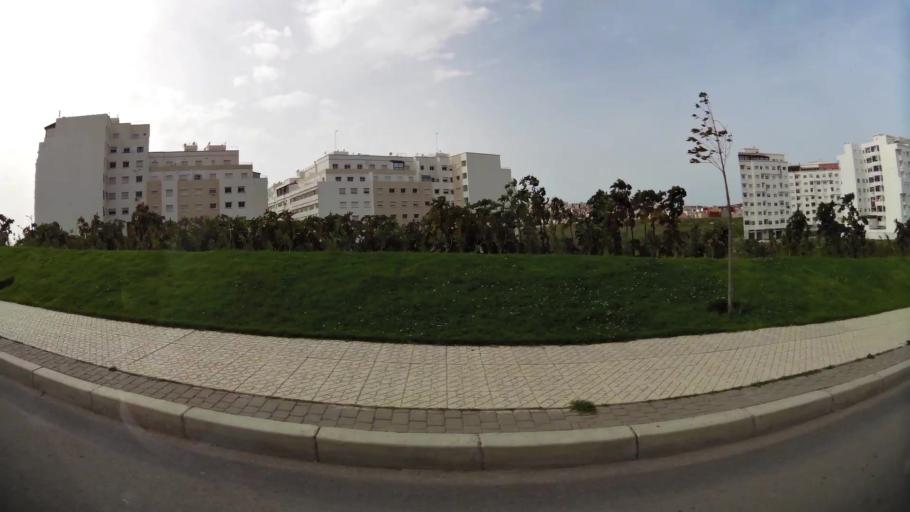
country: MA
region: Tanger-Tetouan
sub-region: Tanger-Assilah
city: Boukhalef
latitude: 35.7445
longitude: -5.8532
